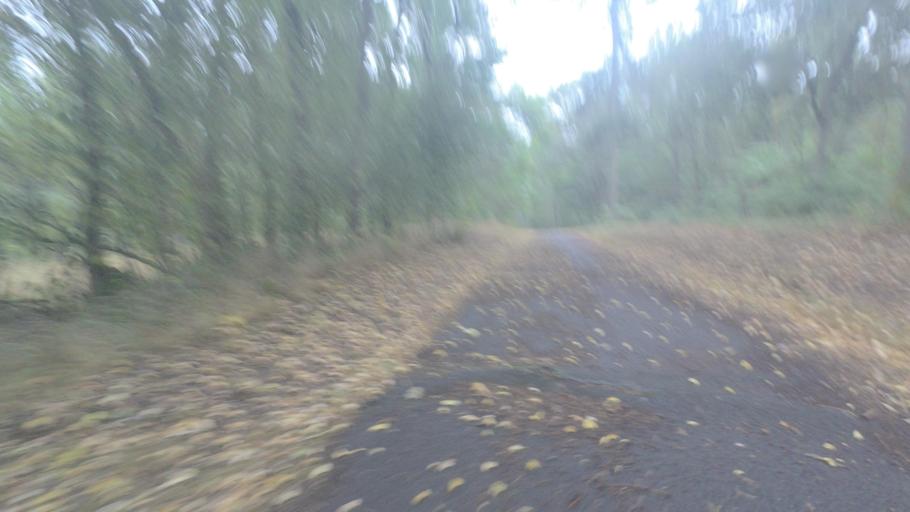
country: DE
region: Brandenburg
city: Heiligengrabe
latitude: 53.1326
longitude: 12.3723
